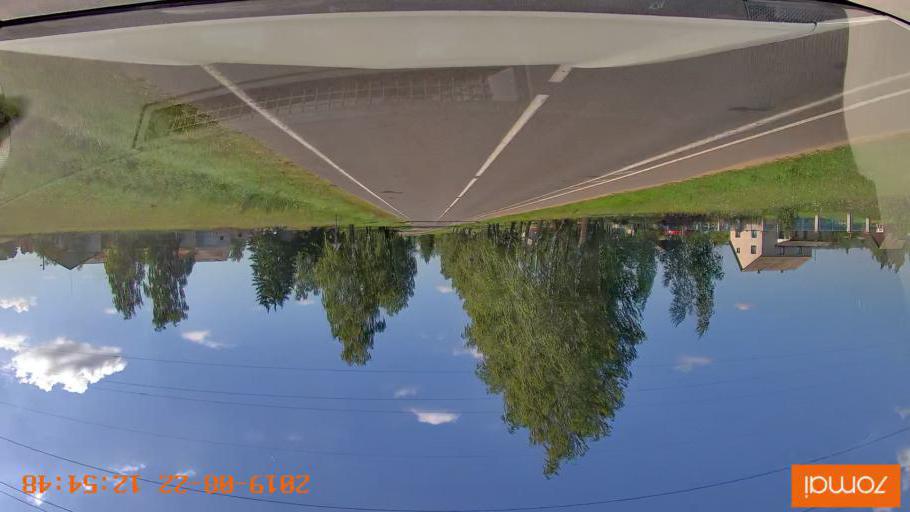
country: BY
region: Minsk
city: Prawdzinski
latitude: 53.4384
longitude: 27.7009
